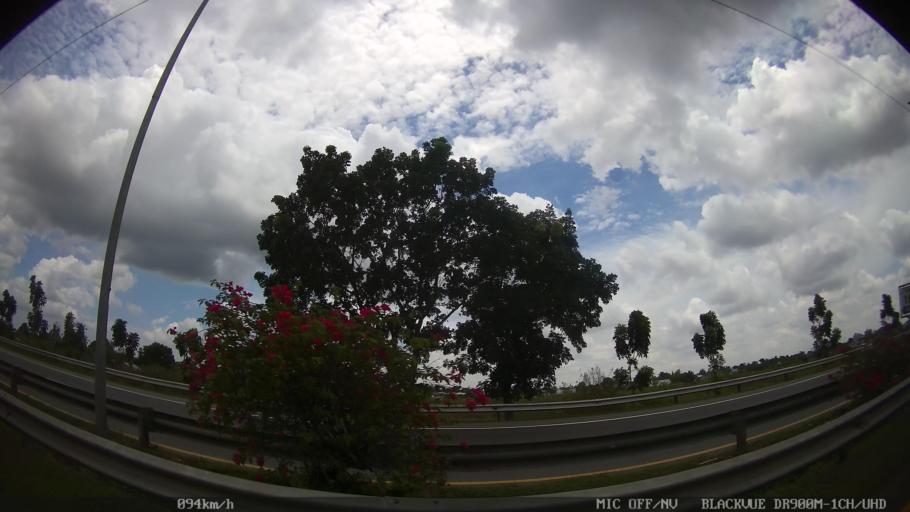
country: ID
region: North Sumatra
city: Medan
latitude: 3.6257
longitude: 98.7193
